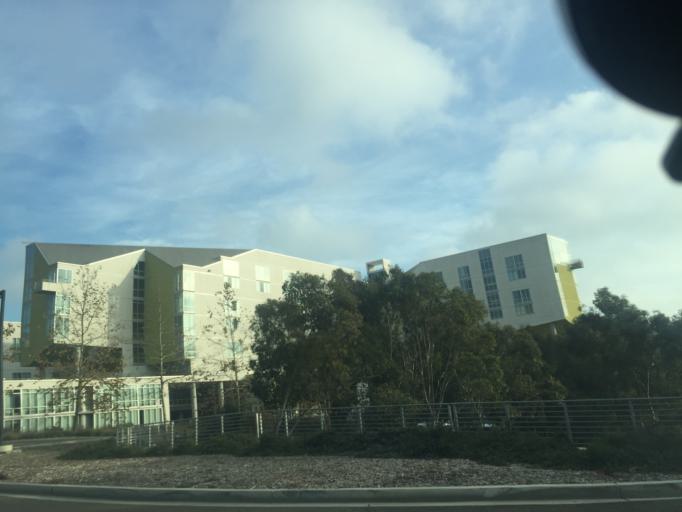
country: US
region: California
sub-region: San Diego County
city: La Jolla
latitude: 32.8731
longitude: -117.2360
